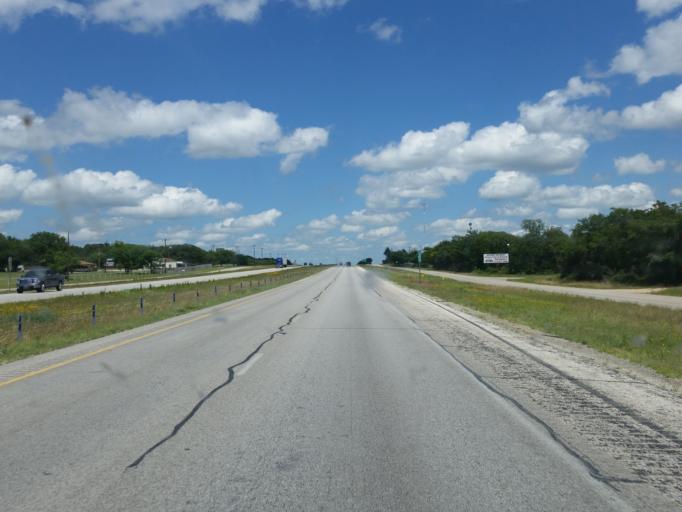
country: US
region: Texas
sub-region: Callahan County
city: Clyde
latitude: 32.4092
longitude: -99.4686
